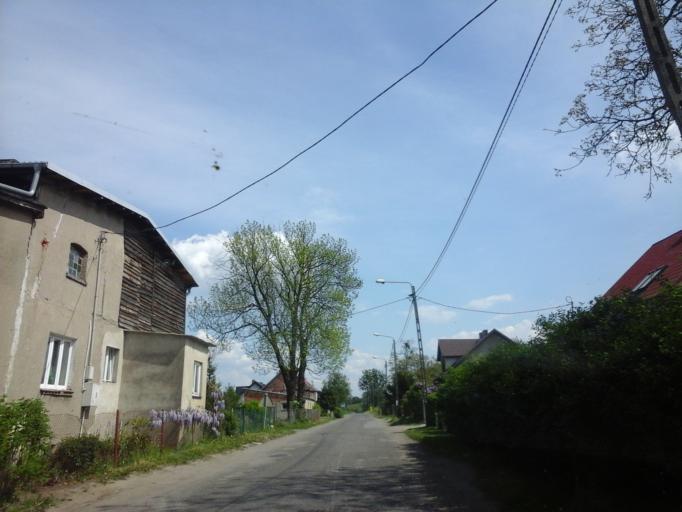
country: PL
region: West Pomeranian Voivodeship
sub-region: Powiat choszczenski
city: Choszczno
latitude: 53.1291
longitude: 15.4084
